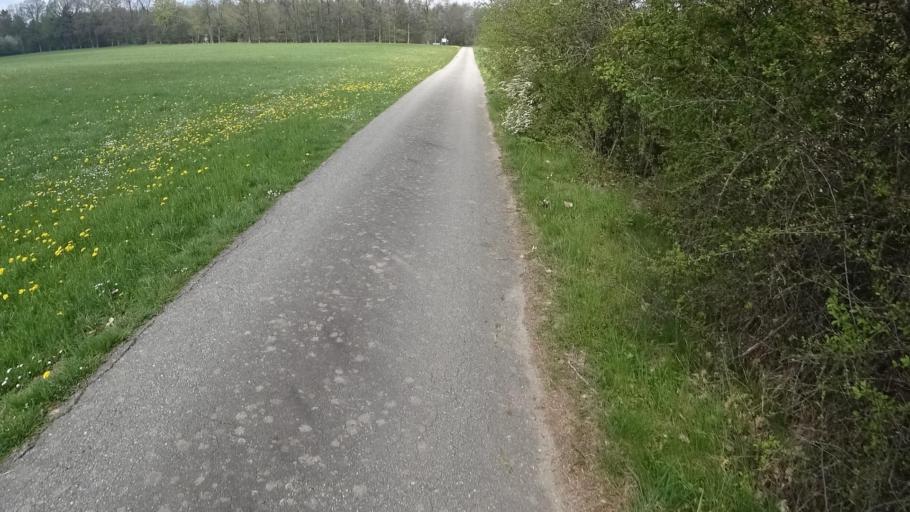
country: DE
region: Rheinland-Pfalz
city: Riegenroth
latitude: 50.0577
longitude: 7.5974
